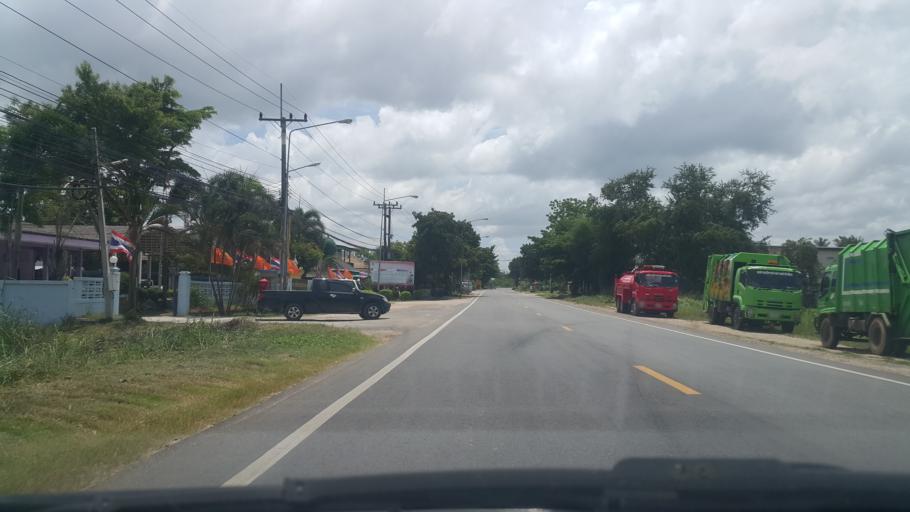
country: TH
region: Rayong
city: Ban Chang
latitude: 12.7689
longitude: 101.0197
